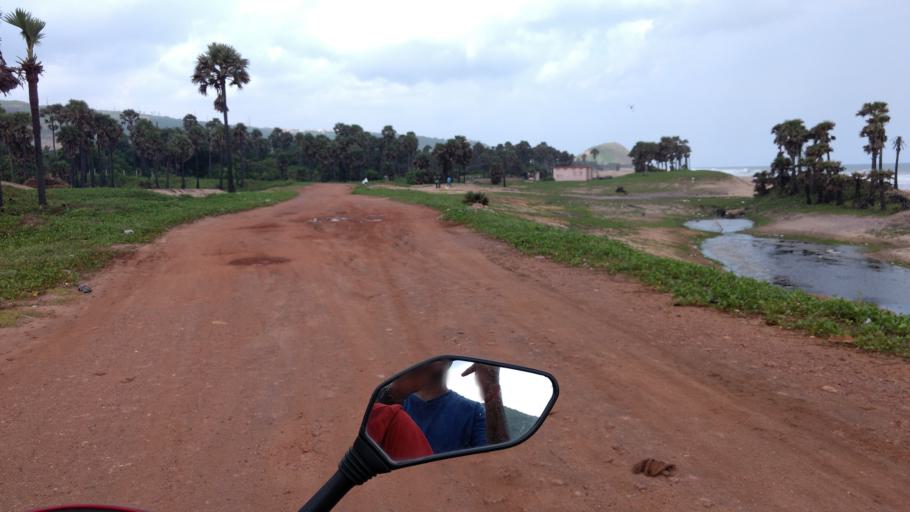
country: IN
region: Andhra Pradesh
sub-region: Vishakhapatnam
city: Yarada
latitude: 17.6522
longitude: 83.2633
